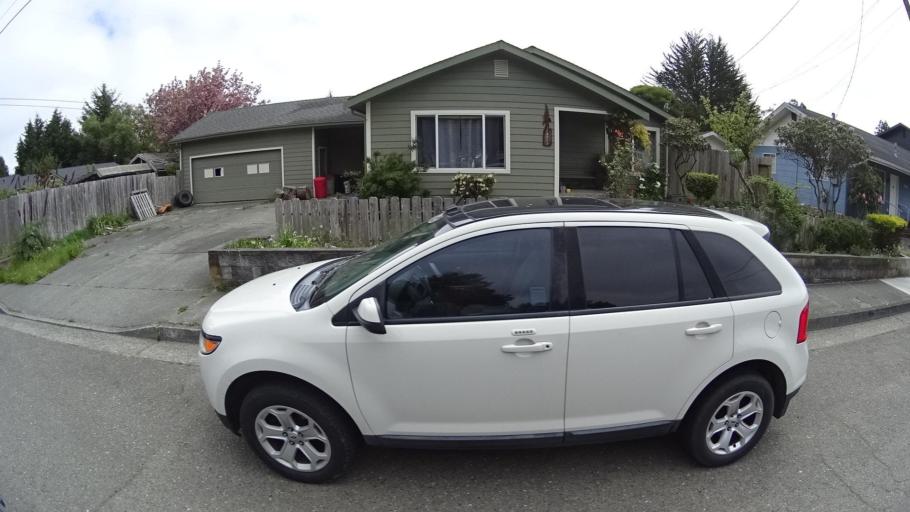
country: US
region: California
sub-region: Humboldt County
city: Cutten
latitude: 40.7605
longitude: -124.1494
